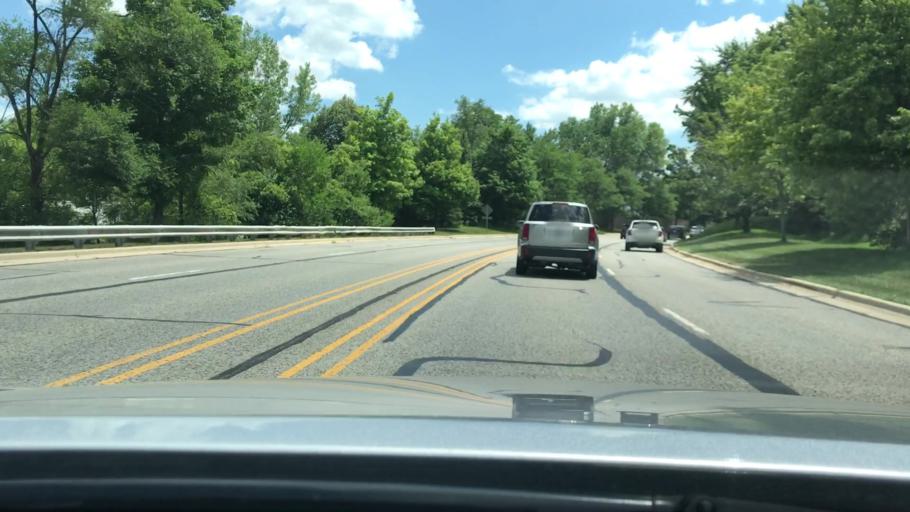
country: US
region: Illinois
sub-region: DuPage County
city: Naperville
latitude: 41.7839
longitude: -88.1107
